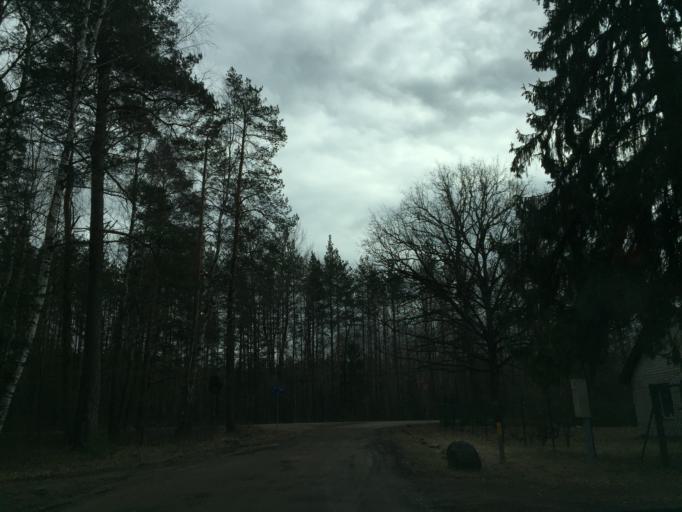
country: LV
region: Garkalne
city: Garkalne
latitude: 57.0740
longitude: 24.4368
